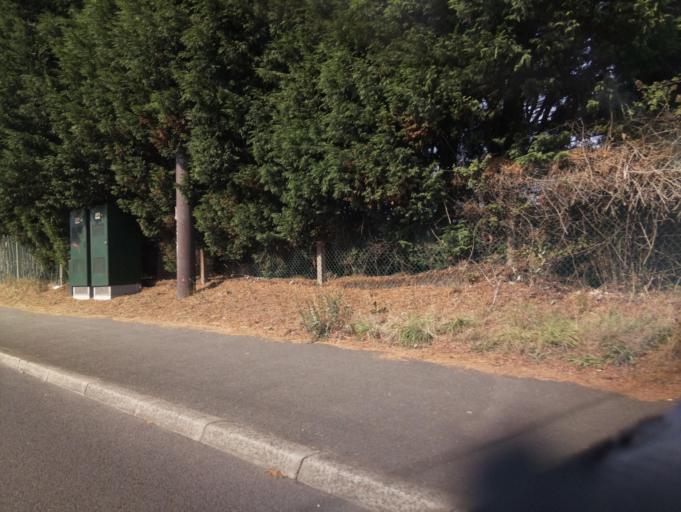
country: GB
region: England
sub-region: Walsall
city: Streetly
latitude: 52.5618
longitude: -1.8928
